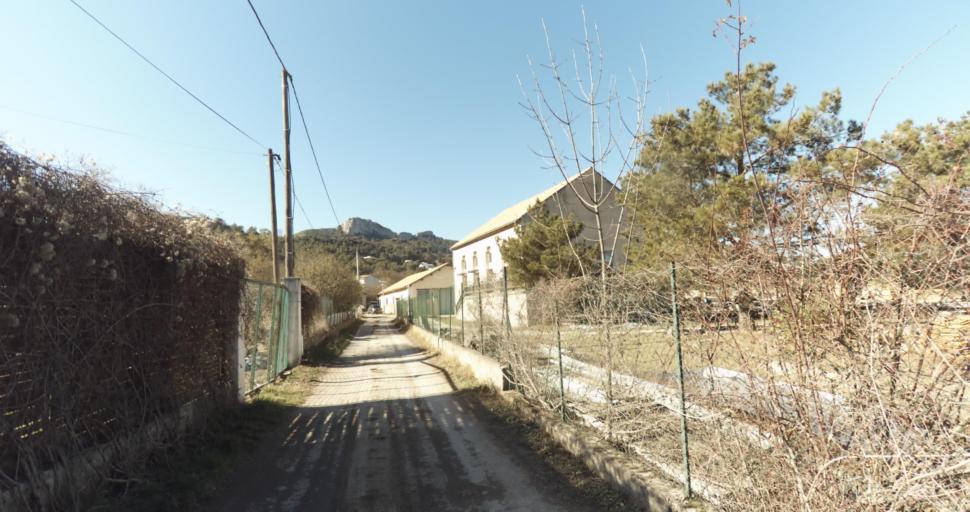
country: FR
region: Provence-Alpes-Cote d'Azur
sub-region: Departement des Bouches-du-Rhone
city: Cadolive
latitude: 43.3891
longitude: 5.5559
